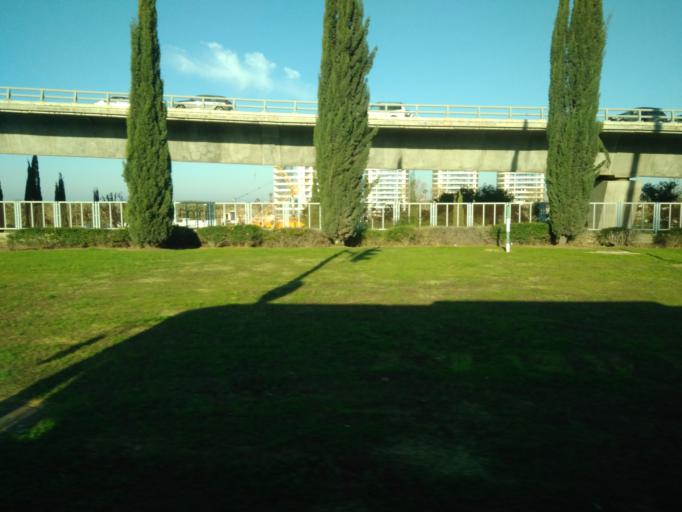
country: IL
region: Tel Aviv
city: Herzliya Pituah
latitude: 32.1418
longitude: 34.8014
